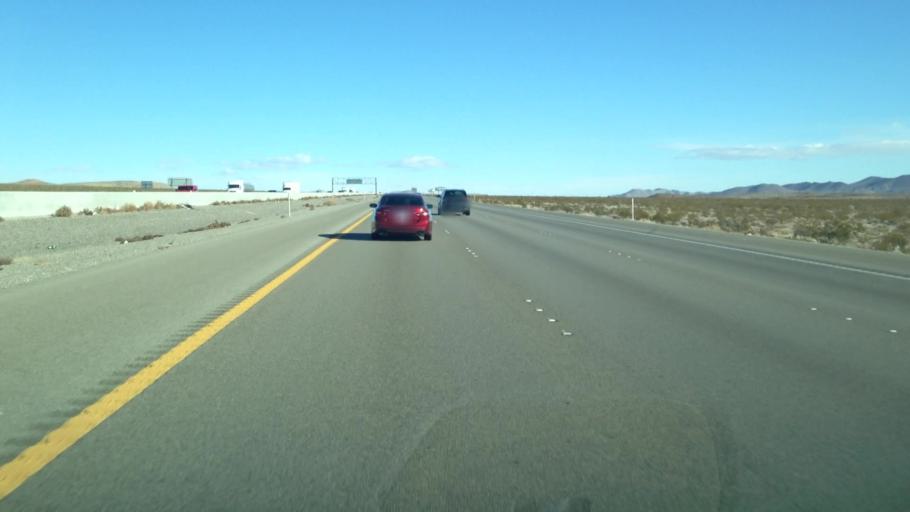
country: US
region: Nevada
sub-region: Clark County
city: Enterprise
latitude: 35.7976
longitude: -115.3158
